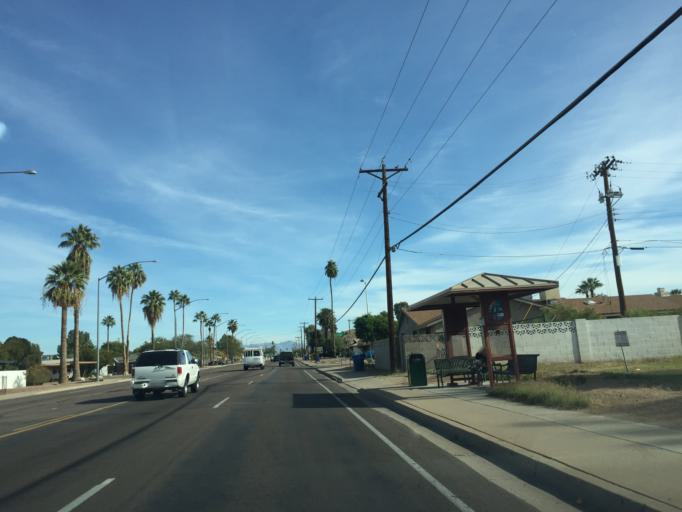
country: US
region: Arizona
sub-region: Maricopa County
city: Mesa
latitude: 33.4079
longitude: -111.7993
